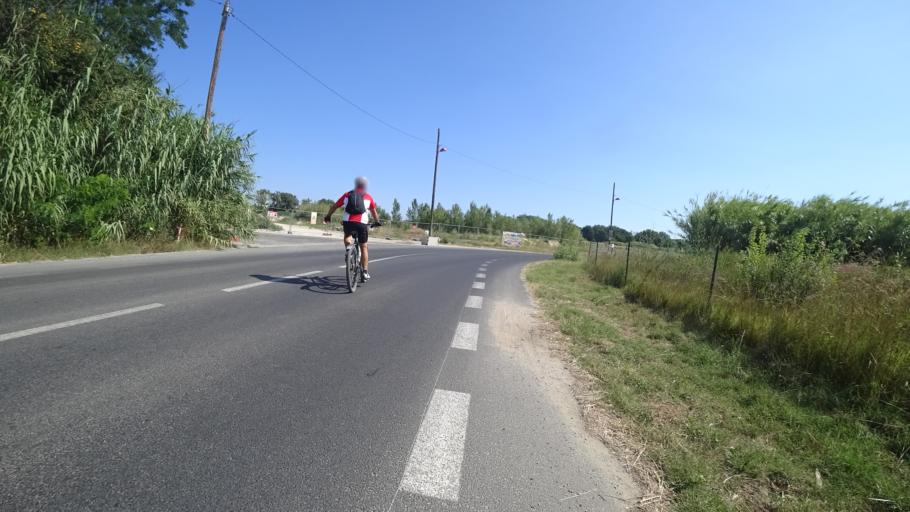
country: FR
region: Languedoc-Roussillon
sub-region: Departement des Pyrenees-Orientales
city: Canet-en-Roussillon
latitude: 42.7066
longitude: 3.0226
